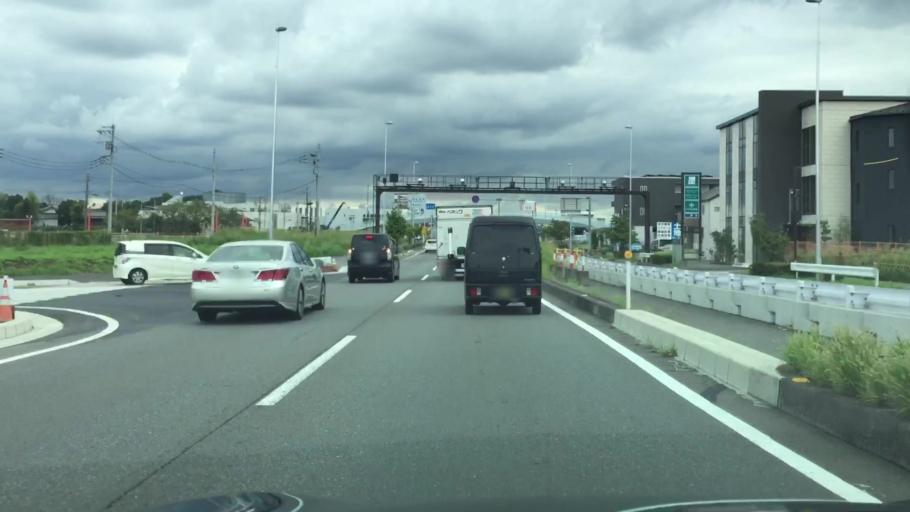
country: JP
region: Saitama
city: Ageoshimo
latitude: 35.9243
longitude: 139.5760
